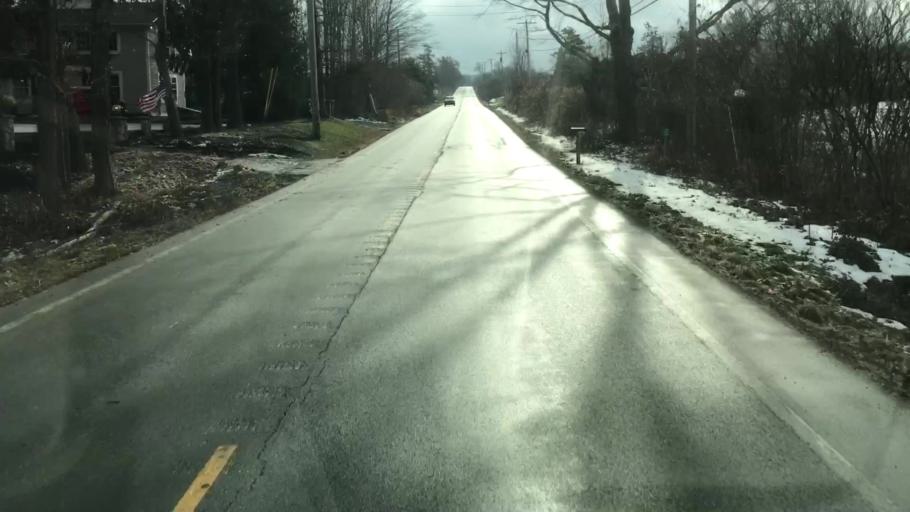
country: US
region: New York
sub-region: Onondaga County
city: Skaneateles
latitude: 42.8598
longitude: -76.3992
